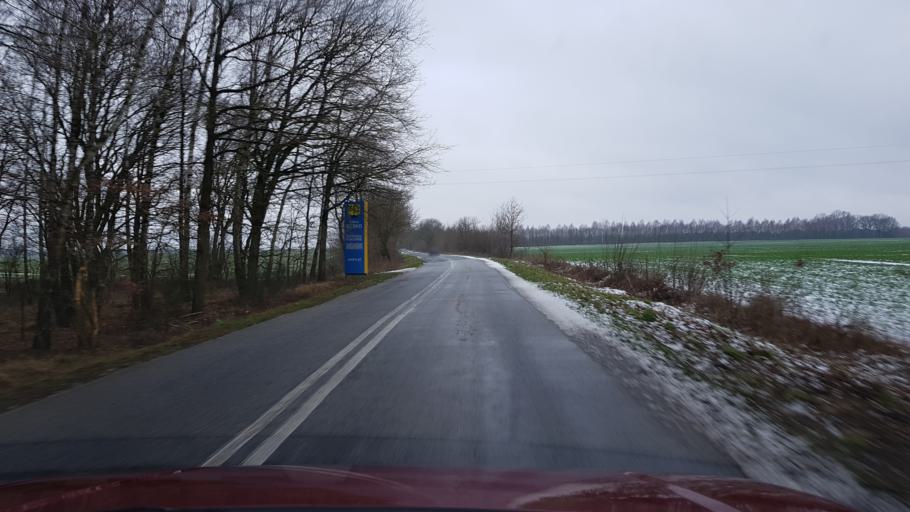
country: PL
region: West Pomeranian Voivodeship
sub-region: Powiat gryficki
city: Ploty
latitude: 53.6921
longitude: 15.2579
